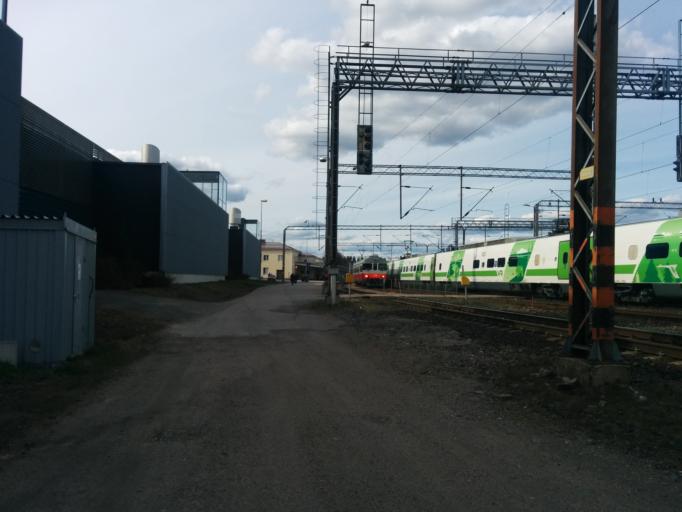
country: FI
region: Haeme
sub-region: Riihimaeki
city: Riihimaeki
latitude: 60.7335
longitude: 24.7822
